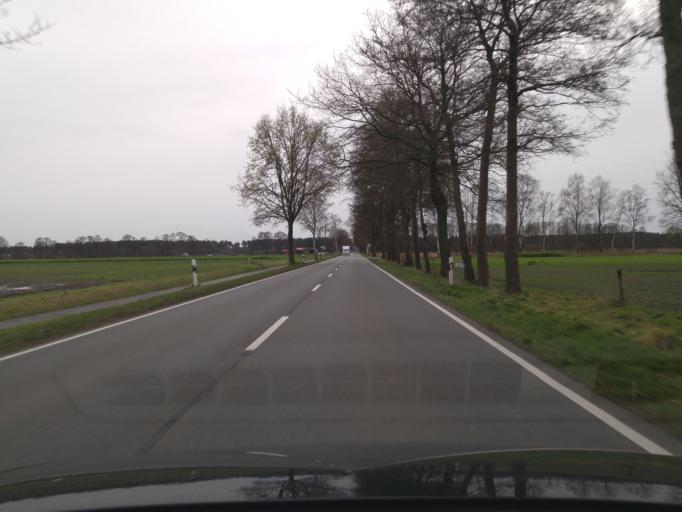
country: DE
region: Lower Saxony
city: Winsen
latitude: 52.7014
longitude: 9.9151
